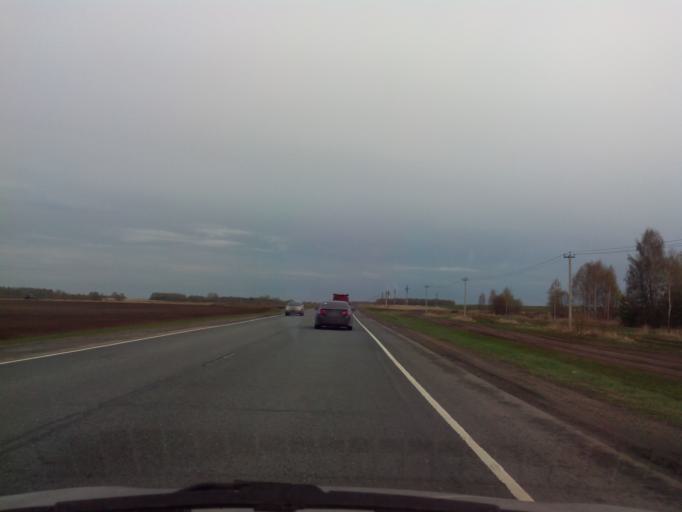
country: RU
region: Moskovskaya
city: Ozherel'ye
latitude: 54.6448
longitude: 38.3657
